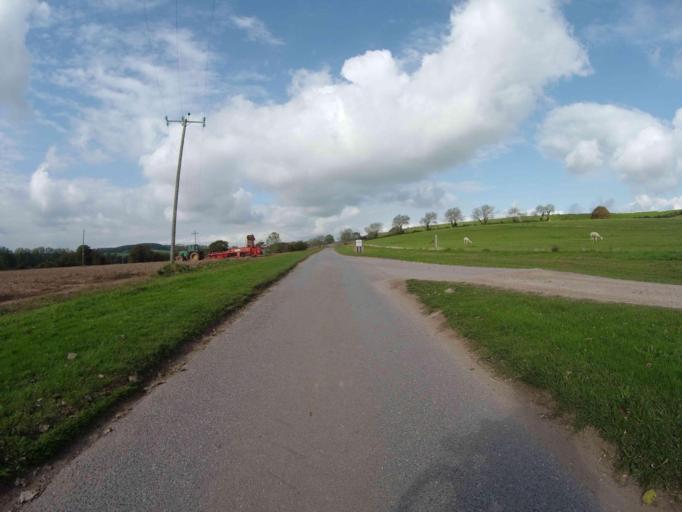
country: GB
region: England
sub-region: Devon
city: Budleigh Salterton
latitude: 50.6379
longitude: -3.3052
